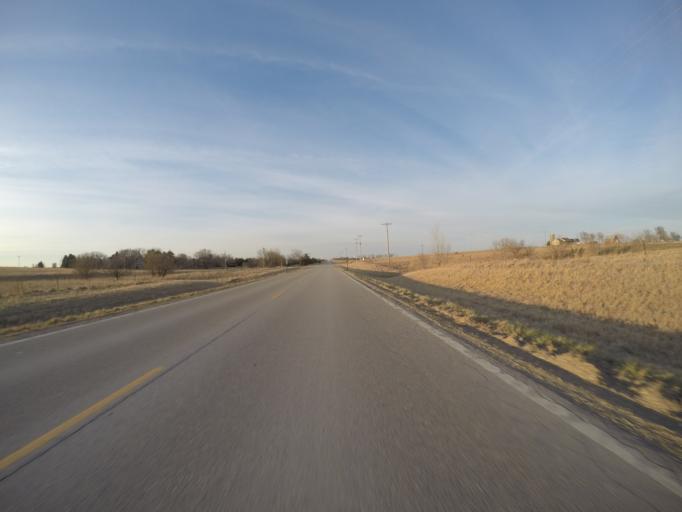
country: US
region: Kansas
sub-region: Riley County
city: Fort Riley North
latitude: 39.3192
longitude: -96.8307
